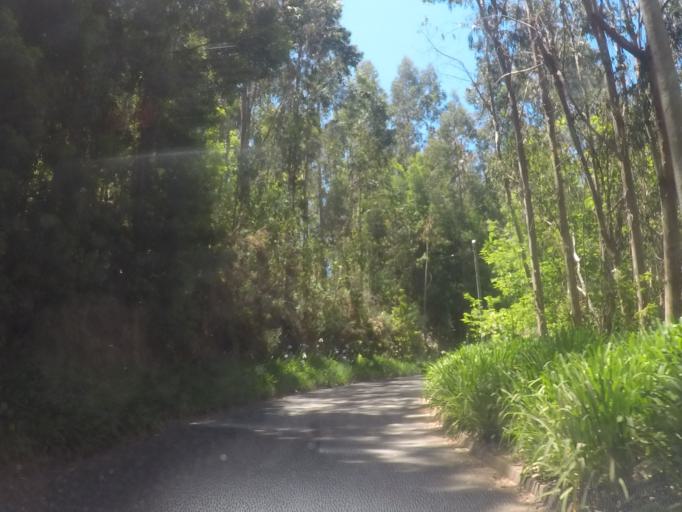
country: PT
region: Madeira
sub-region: Camara de Lobos
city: Curral das Freiras
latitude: 32.6950
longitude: -16.9779
